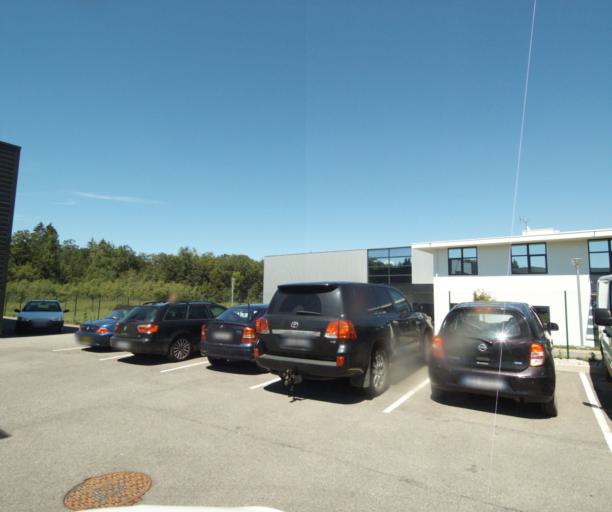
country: FR
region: Rhone-Alpes
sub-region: Departement de la Haute-Savoie
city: Ballaison
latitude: 46.2777
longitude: 6.3458
